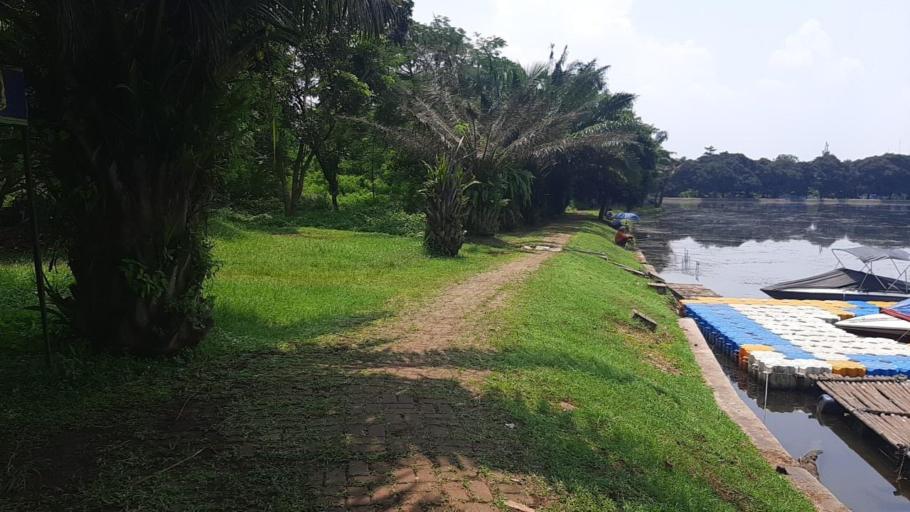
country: ID
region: West Java
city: Cileungsir
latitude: -6.4091
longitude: 106.9956
